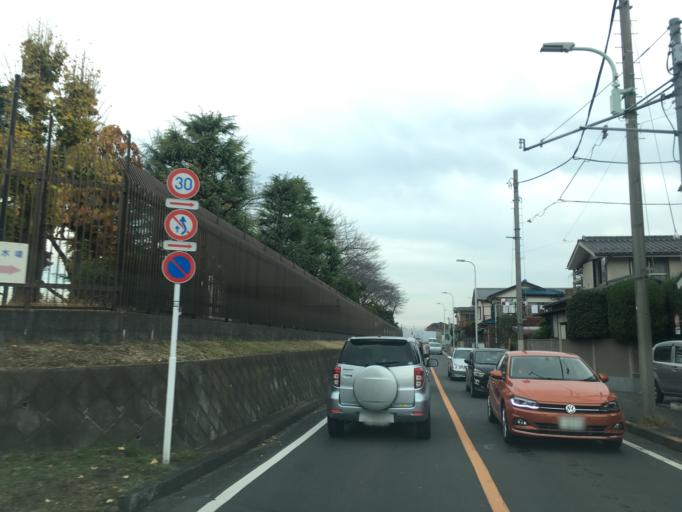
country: JP
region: Tokyo
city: Higashimurayama-shi
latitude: 35.7524
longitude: 139.4620
